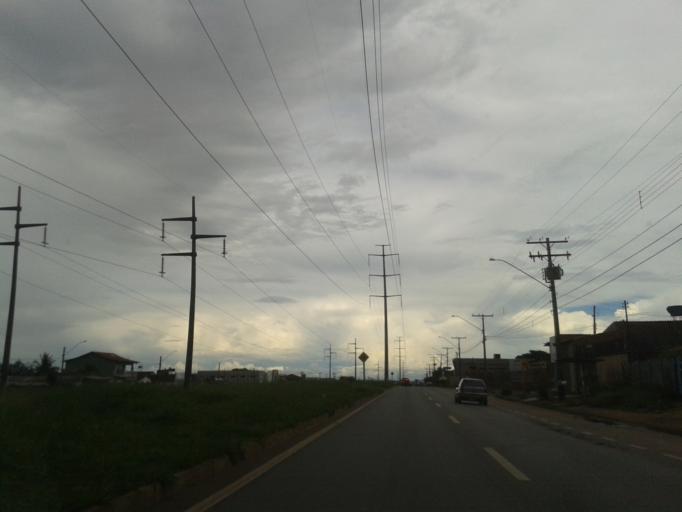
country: BR
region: Goias
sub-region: Aparecida De Goiania
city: Aparecida de Goiania
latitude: -16.7819
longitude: -49.2803
